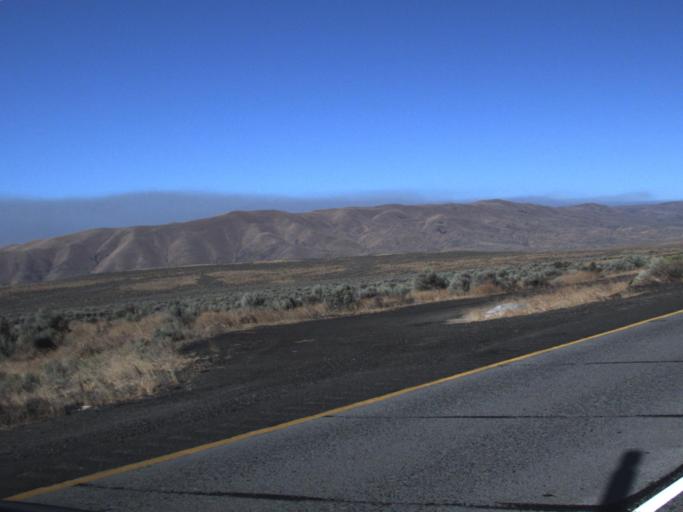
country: US
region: Washington
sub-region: Kittitas County
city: Kittitas
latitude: 46.8467
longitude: -120.3832
